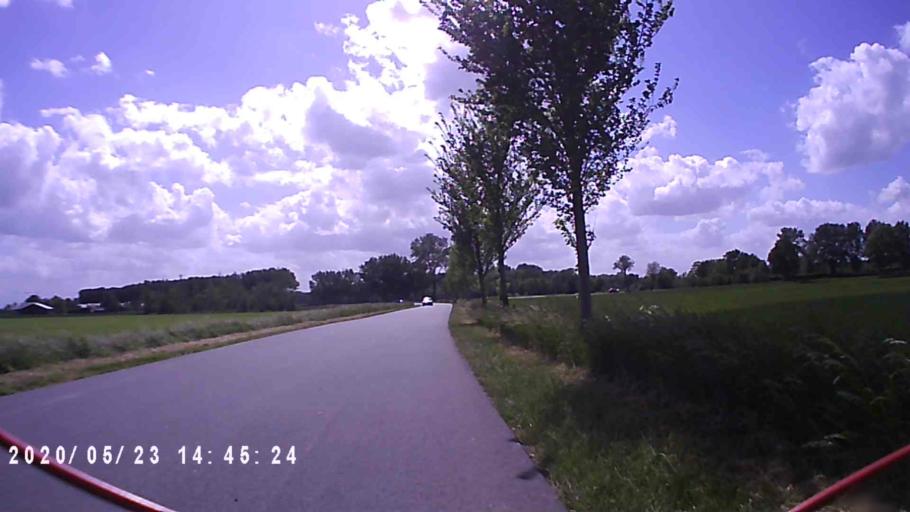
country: NL
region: Groningen
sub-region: Gemeente Delfzijl
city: Delfzijl
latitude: 53.2644
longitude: 6.9536
